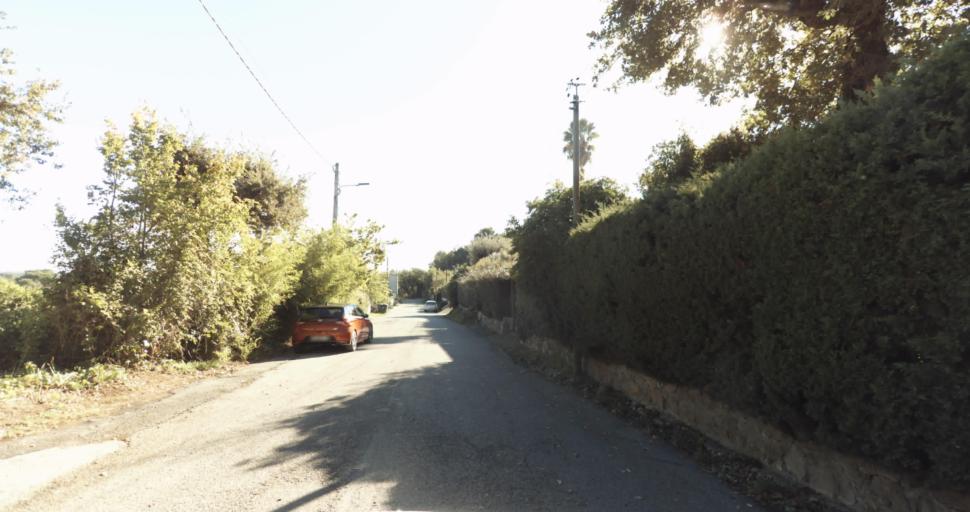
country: FR
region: Provence-Alpes-Cote d'Azur
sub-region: Departement des Alpes-Maritimes
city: Vence
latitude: 43.7166
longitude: 7.1125
